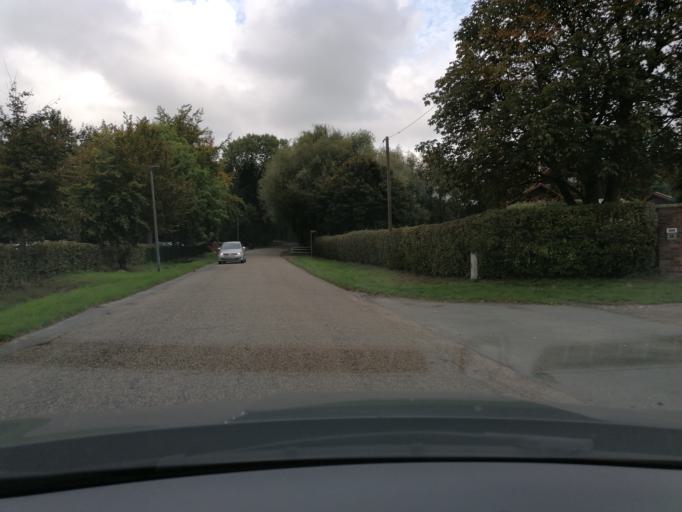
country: DE
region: North Rhine-Westphalia
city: Herten
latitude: 51.5784
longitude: 7.0930
